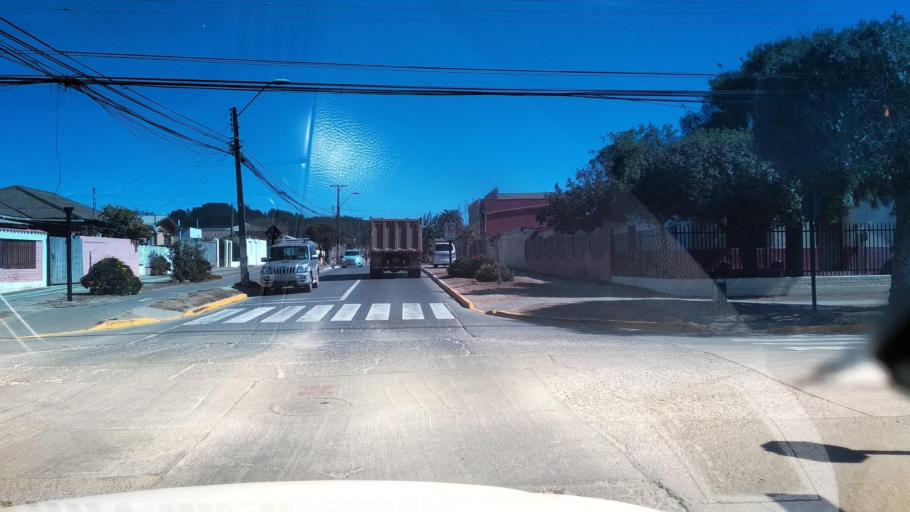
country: CL
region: O'Higgins
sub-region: Provincia de Colchagua
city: Santa Cruz
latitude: -34.3906
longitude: -72.0041
